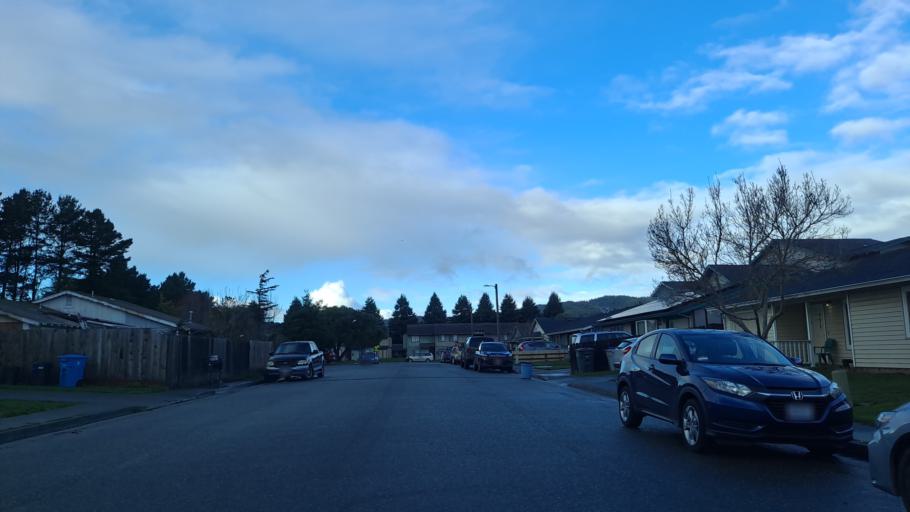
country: US
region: California
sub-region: Humboldt County
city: Fortuna
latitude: 40.5837
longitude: -124.1409
